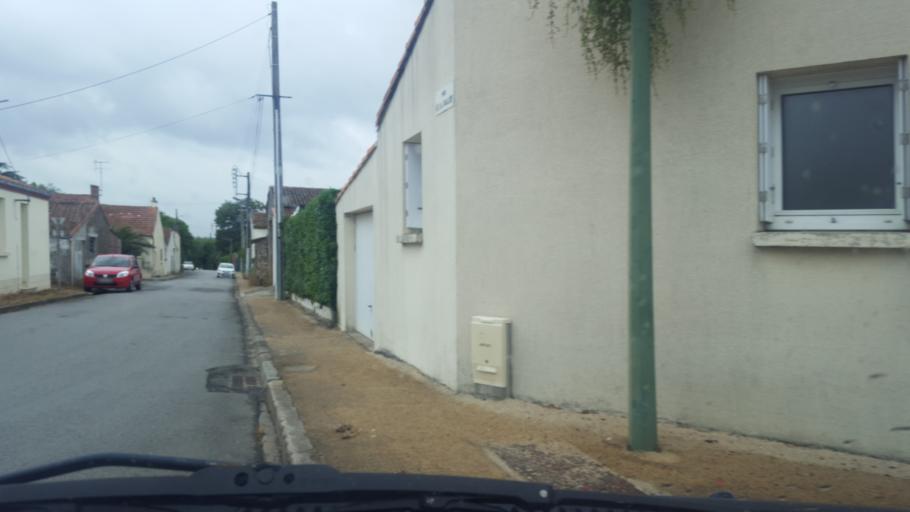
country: FR
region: Pays de la Loire
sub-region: Departement de la Loire-Atlantique
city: Saint-Lumine-de-Coutais
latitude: 47.0560
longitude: -1.7264
